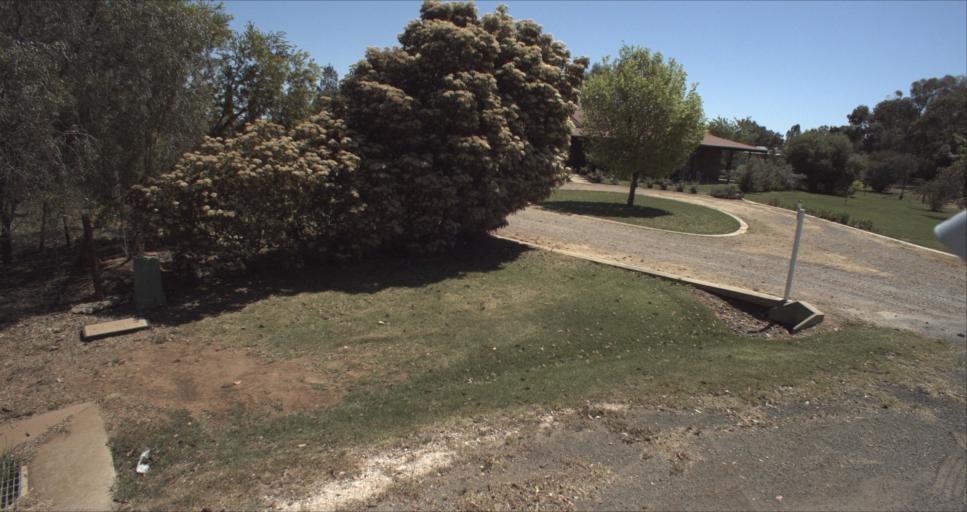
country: AU
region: New South Wales
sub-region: Leeton
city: Leeton
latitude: -34.5246
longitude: 146.4059
